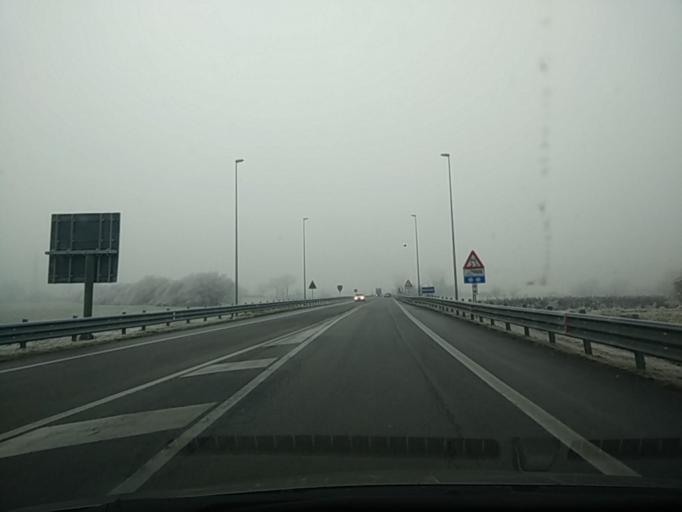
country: IT
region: Veneto
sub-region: Provincia di Belluno
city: Seren del Grappa
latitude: 46.0024
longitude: 11.8351
